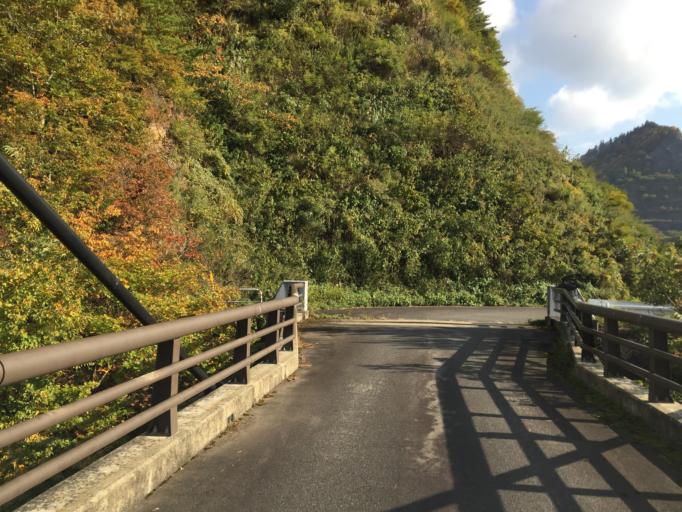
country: JP
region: Fukushima
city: Kitakata
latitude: 37.7553
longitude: 139.9134
